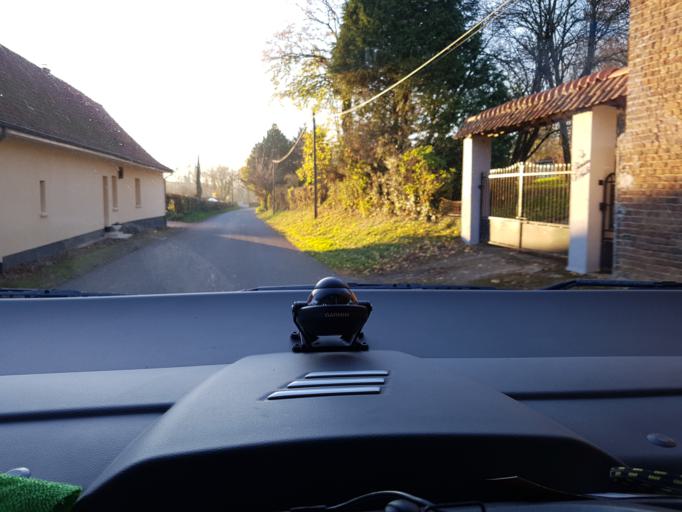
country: FR
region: Nord-Pas-de-Calais
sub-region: Departement du Pas-de-Calais
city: Beaurainville
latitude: 50.5135
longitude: 1.9306
